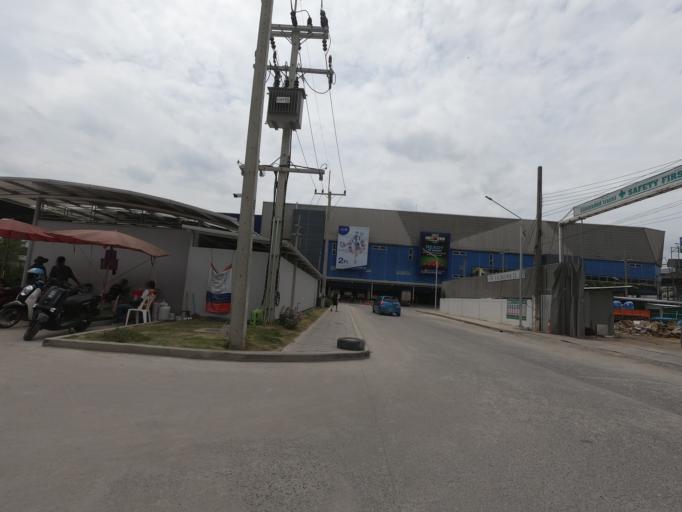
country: TH
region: Bangkok
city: Sai Mai
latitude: 13.9583
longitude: 100.6411
